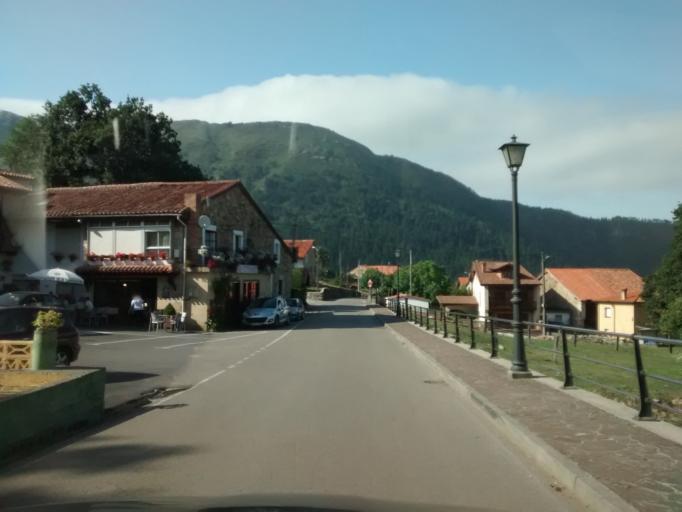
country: ES
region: Cantabria
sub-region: Provincia de Cantabria
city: Ruente
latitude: 43.2629
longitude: -4.2489
